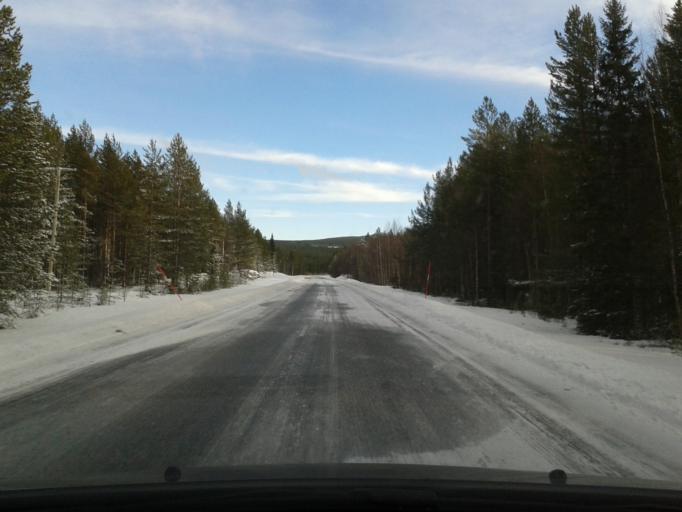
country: SE
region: Vaesterbotten
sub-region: Asele Kommun
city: Asele
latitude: 64.3405
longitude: 17.0265
